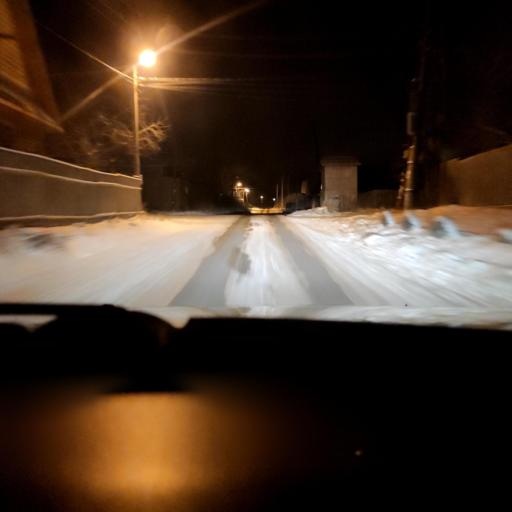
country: RU
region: Perm
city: Kondratovo
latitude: 58.0482
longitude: 56.0468
